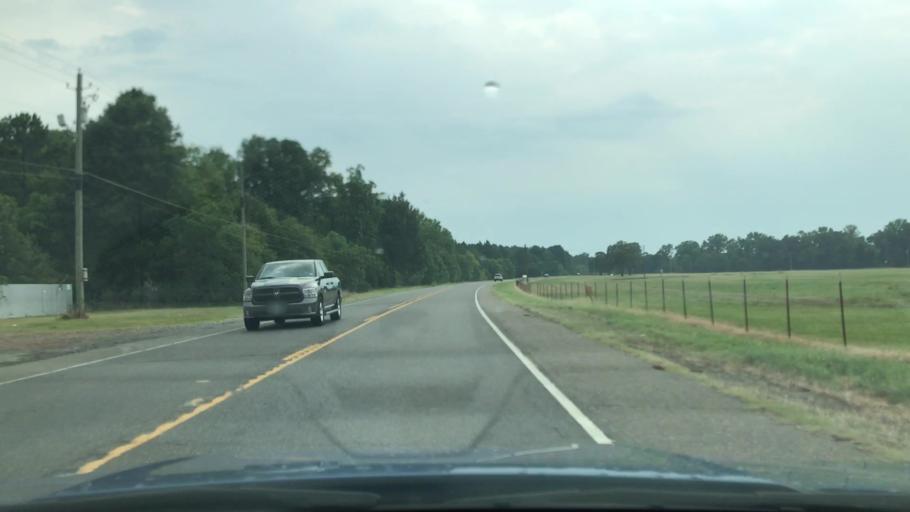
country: US
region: Texas
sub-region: Harrison County
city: Waskom
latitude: 32.4607
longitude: -94.0263
